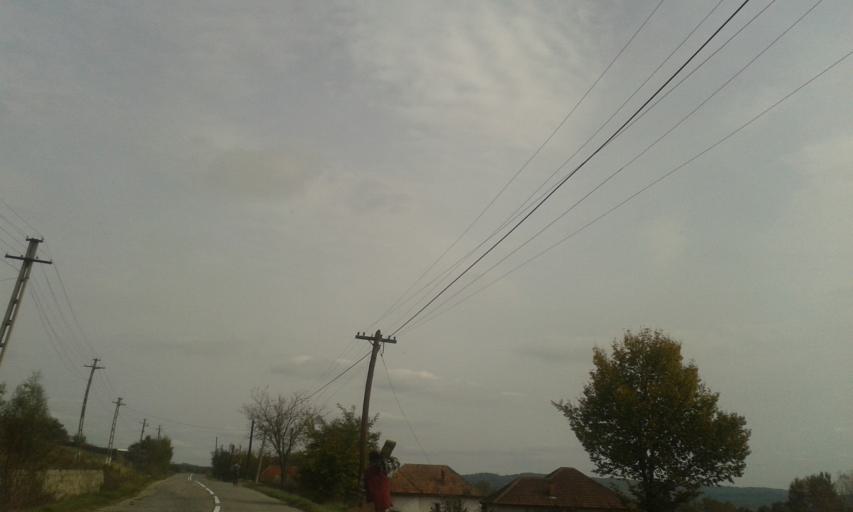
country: RO
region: Valcea
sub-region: Comuna Gradistea
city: Gradistea
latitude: 44.9001
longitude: 23.8124
